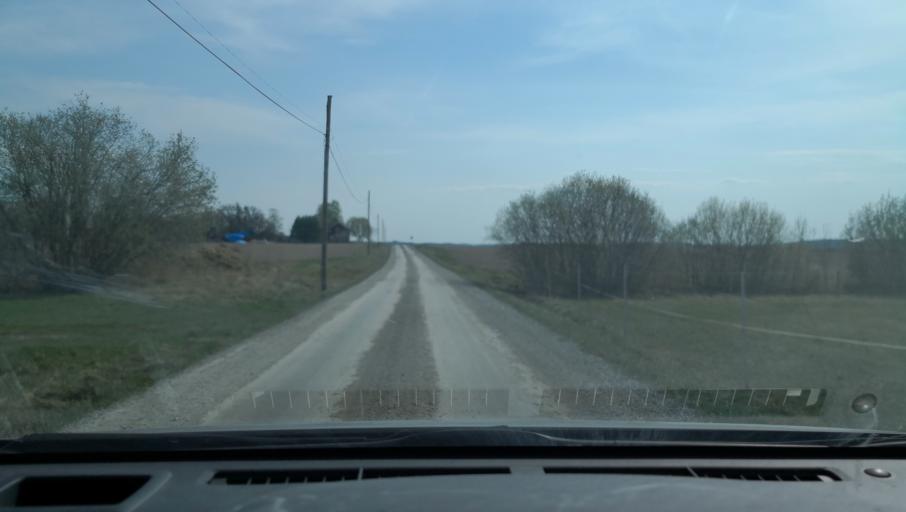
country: SE
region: Vaestmanland
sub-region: Vasteras
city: Skultuna
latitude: 59.7943
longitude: 16.4398
